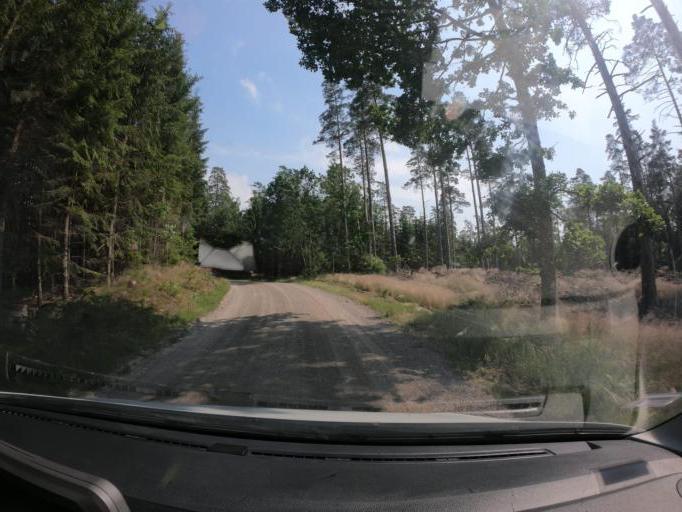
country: SE
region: Kronoberg
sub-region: Markaryds Kommun
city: Markaryd
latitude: 56.3773
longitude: 13.5578
